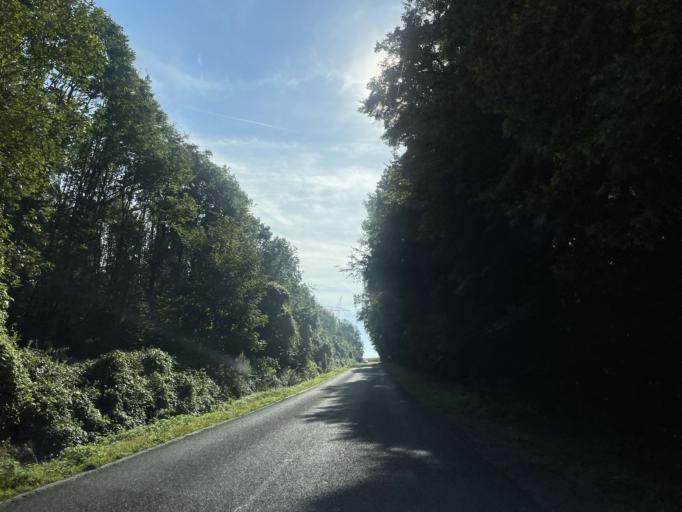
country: FR
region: Ile-de-France
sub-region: Departement de Seine-et-Marne
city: Saint-Jean-les-Deux-Jumeaux
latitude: 48.9501
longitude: 2.9904
